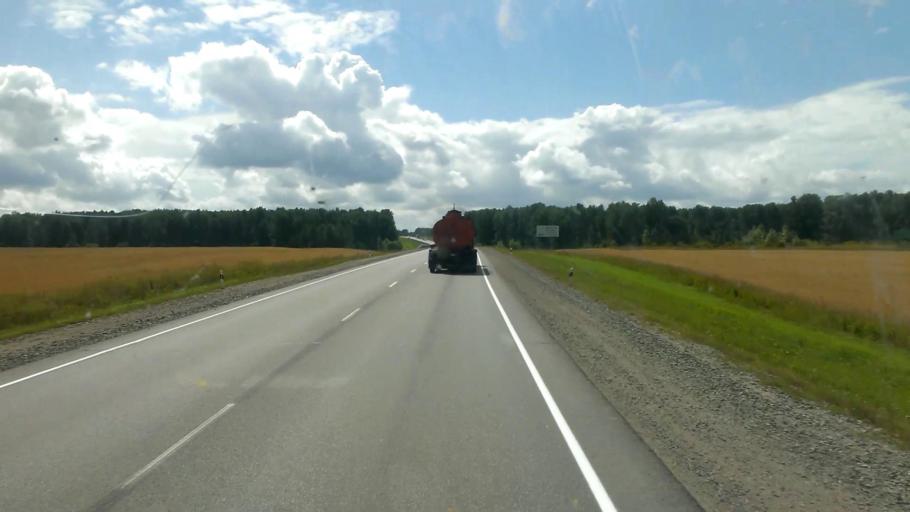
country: RU
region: Altai Krai
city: Troitskoye
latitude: 52.9865
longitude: 84.7435
